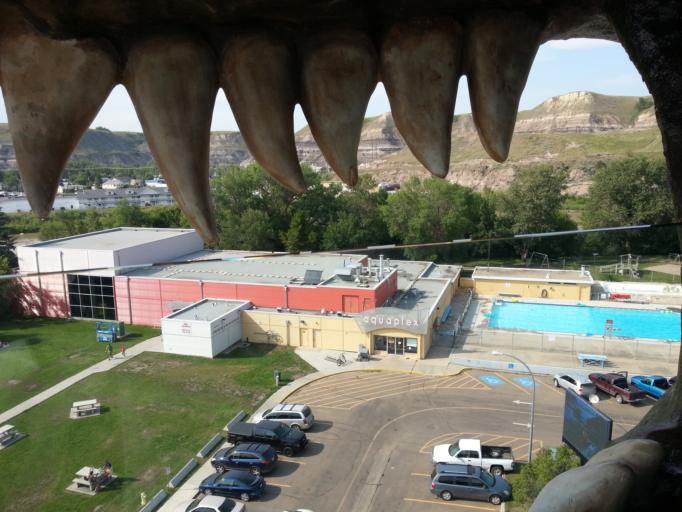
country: CA
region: Alberta
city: Three Hills
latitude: 51.4671
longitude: -112.7093
